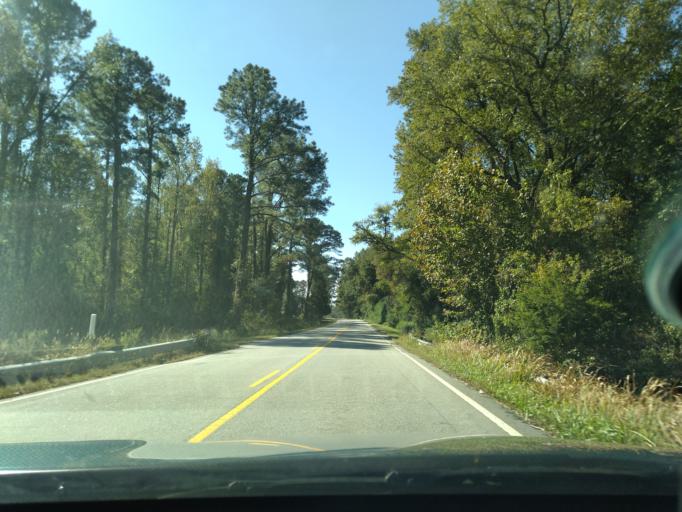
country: US
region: North Carolina
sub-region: Washington County
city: Plymouth
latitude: 35.7307
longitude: -76.7463
